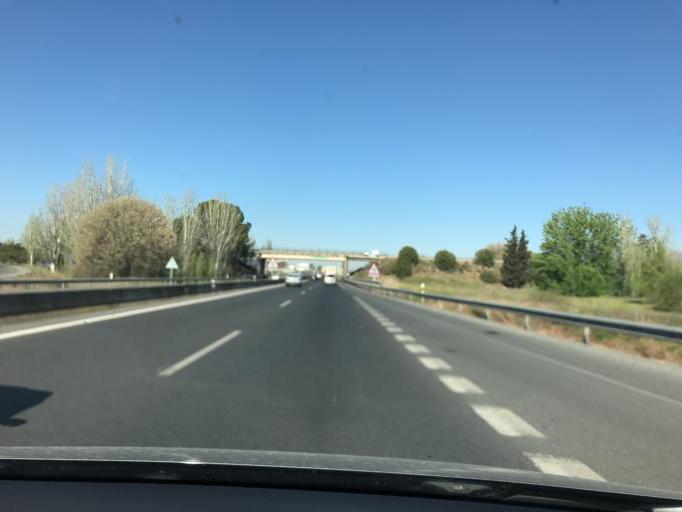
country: ES
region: Andalusia
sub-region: Provincia de Granada
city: Chauchina
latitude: 37.1914
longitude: -3.7487
